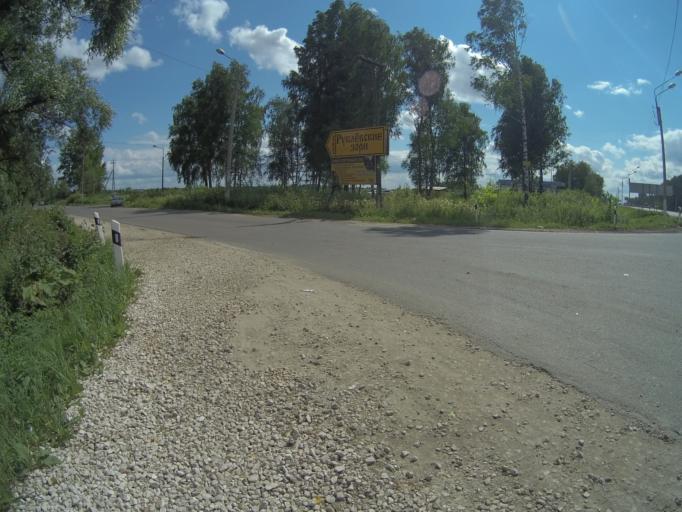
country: RU
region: Vladimir
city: Vorsha
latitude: 56.0737
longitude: 40.1723
